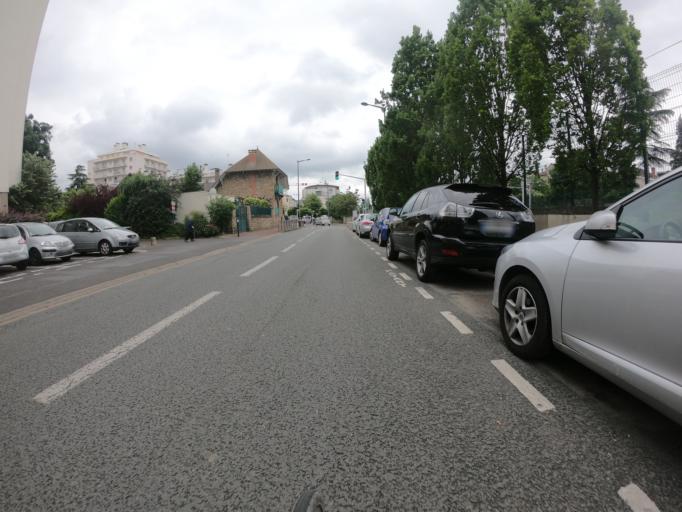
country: FR
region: Ile-de-France
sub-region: Departement des Hauts-de-Seine
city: Antony
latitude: 48.7585
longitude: 2.3030
